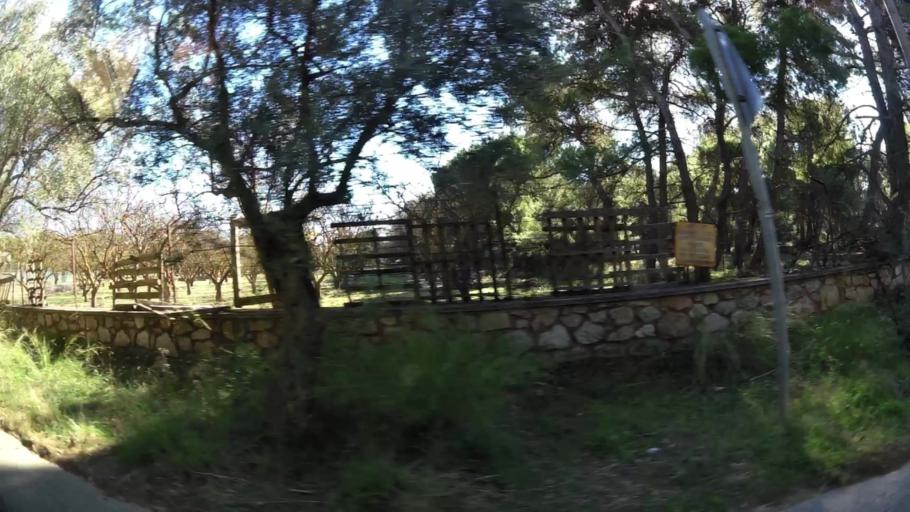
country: GR
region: Attica
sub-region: Nomarchia Anatolikis Attikis
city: Varybobi
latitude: 38.1225
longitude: 23.7924
